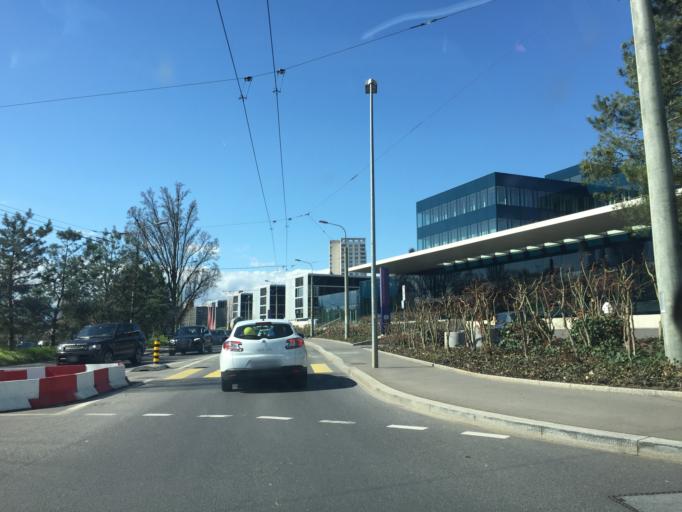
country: CH
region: Vaud
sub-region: Lausanne District
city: Lausanne
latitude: 46.5143
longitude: 6.6114
